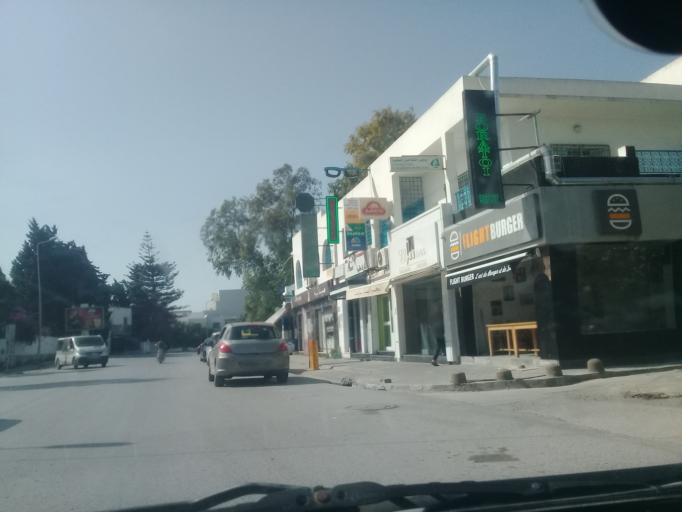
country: TN
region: Tunis
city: Al Marsa
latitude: 36.8822
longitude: 10.3248
